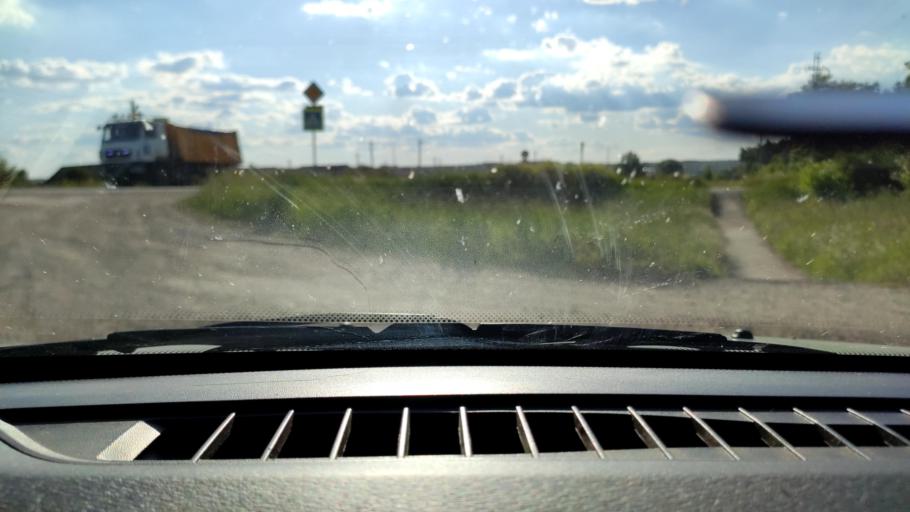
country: RU
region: Perm
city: Orda
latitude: 57.1875
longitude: 56.9162
